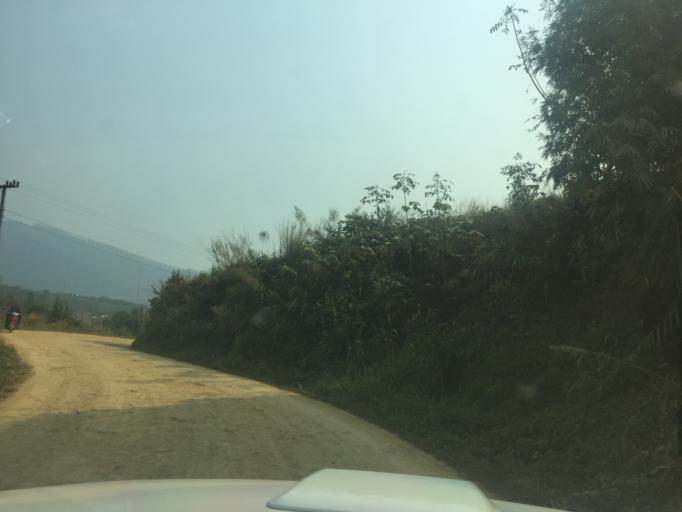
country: TH
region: Phayao
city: Phu Sang
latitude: 19.6712
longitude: 100.5238
